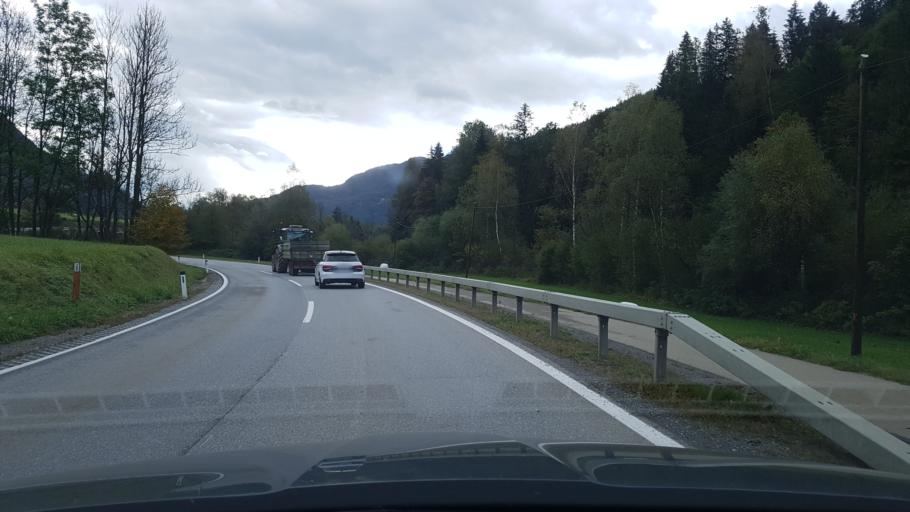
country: AT
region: Styria
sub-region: Politischer Bezirk Murau
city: Oberwolz Stadt
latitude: 47.1539
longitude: 14.2613
